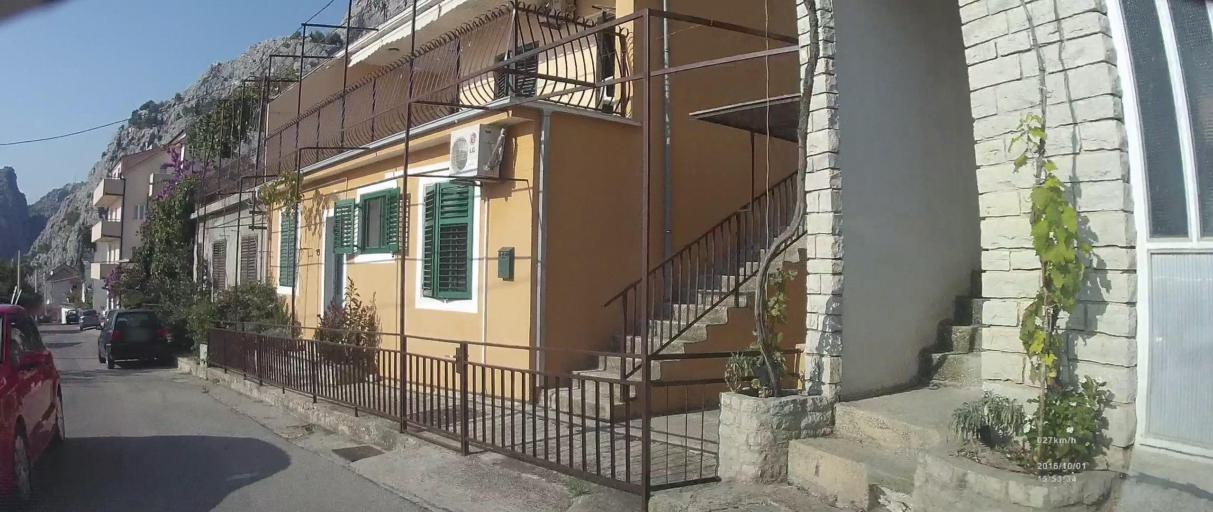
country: HR
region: Splitsko-Dalmatinska
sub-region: Grad Omis
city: Omis
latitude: 43.4403
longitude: 16.7002
